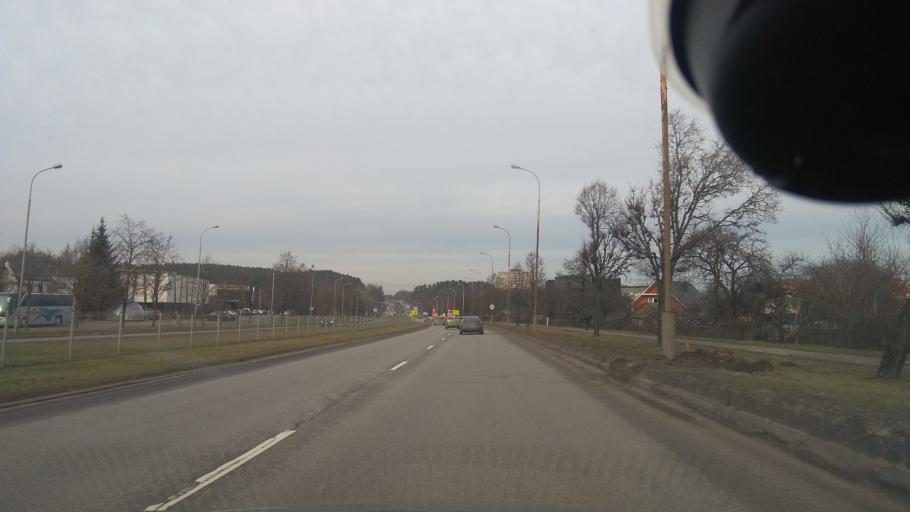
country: LT
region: Vilnius County
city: Seskine
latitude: 54.7182
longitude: 25.2712
